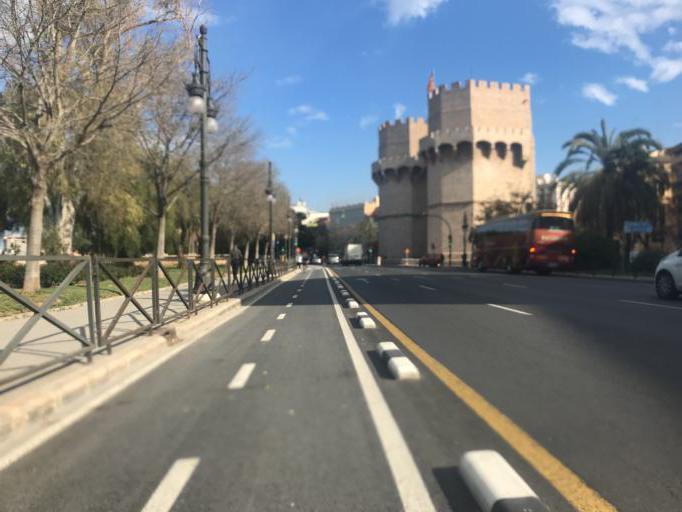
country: ES
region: Valencia
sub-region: Provincia de Valencia
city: Valencia
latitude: 39.4801
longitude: -0.3770
